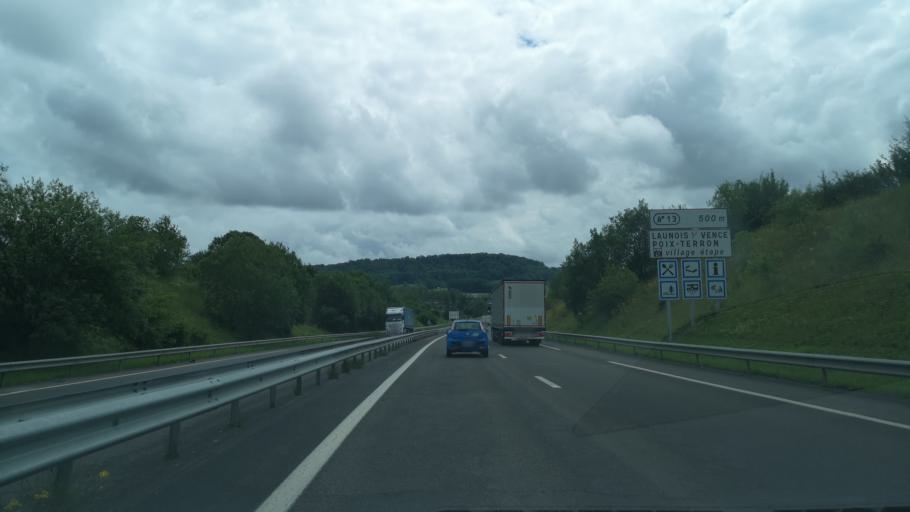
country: FR
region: Champagne-Ardenne
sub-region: Departement des Ardennes
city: La Francheville
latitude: 49.6513
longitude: 4.6337
